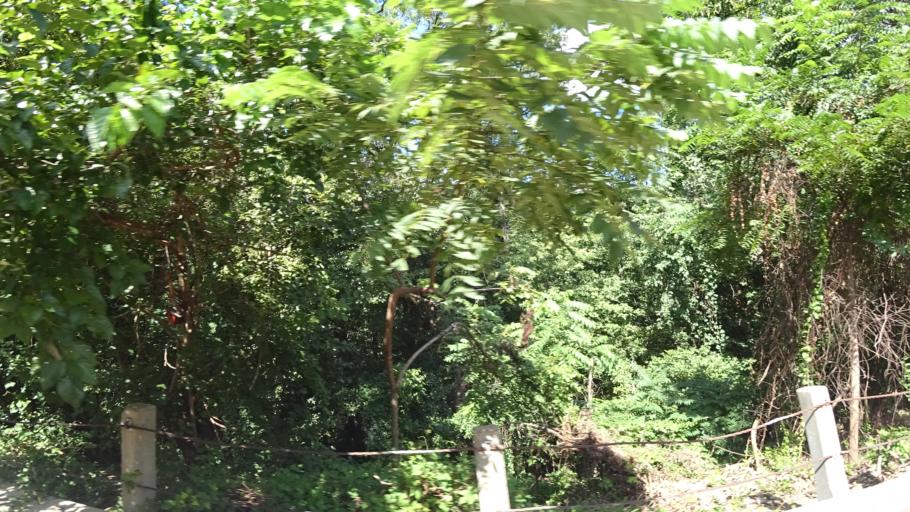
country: US
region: Washington, D.C.
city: Washington, D.C.
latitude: 38.9354
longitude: -77.0431
